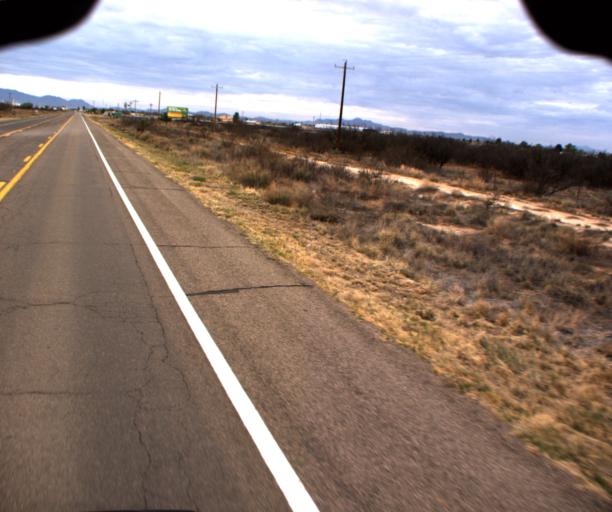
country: US
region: Arizona
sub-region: Cochise County
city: Willcox
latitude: 32.2706
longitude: -109.8201
